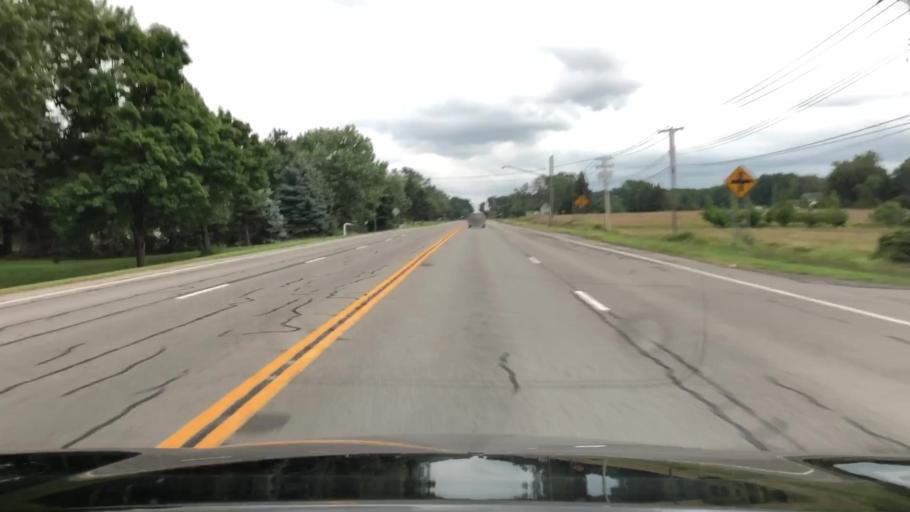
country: US
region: New York
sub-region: Erie County
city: Orchard Park
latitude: 42.8043
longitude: -78.6969
